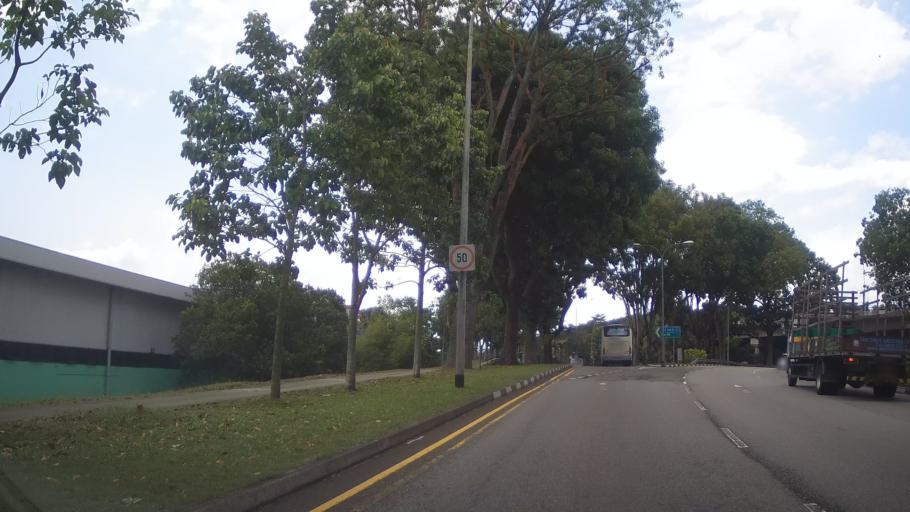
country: MY
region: Johor
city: Johor Bahru
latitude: 1.3303
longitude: 103.6763
